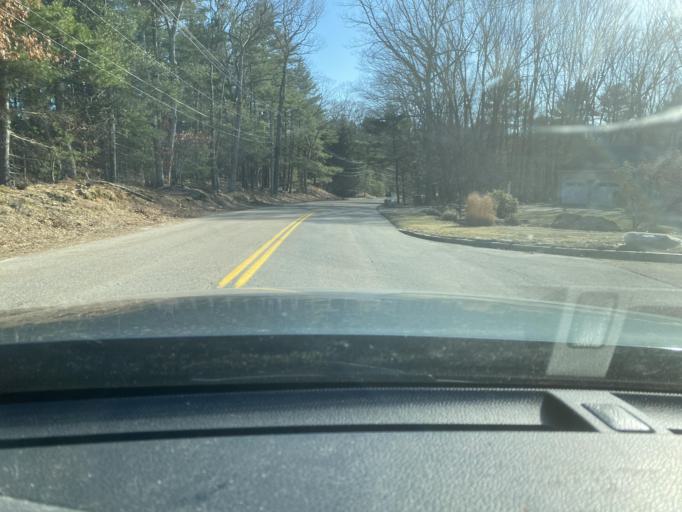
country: US
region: Massachusetts
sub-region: Middlesex County
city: Holliston
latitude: 42.2065
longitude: -71.3914
